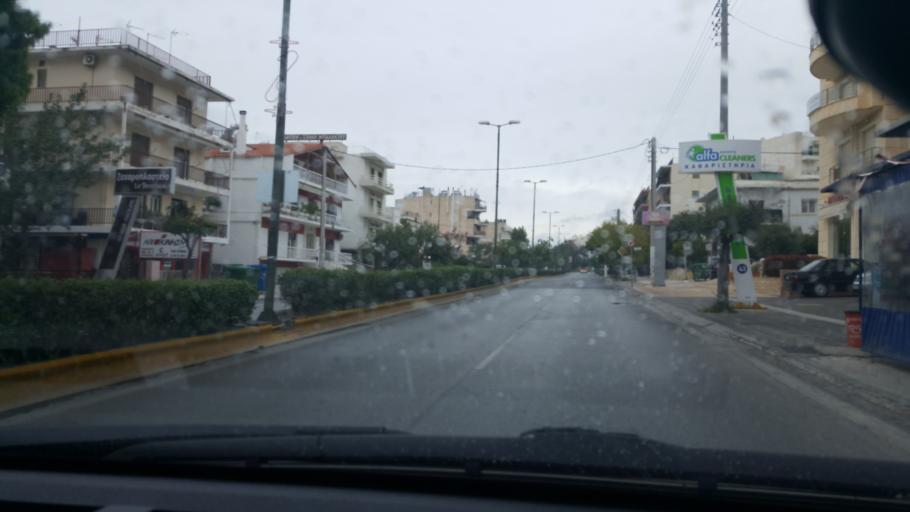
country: GR
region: Attica
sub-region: Nomarchia Athinas
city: Ilioupoli
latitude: 37.9332
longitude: 23.7589
